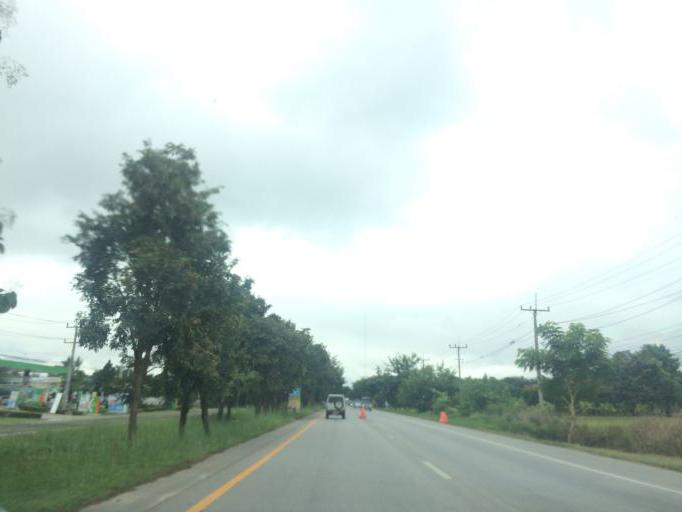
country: TH
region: Chiang Rai
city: Mae Lao
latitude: 19.7533
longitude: 99.7312
